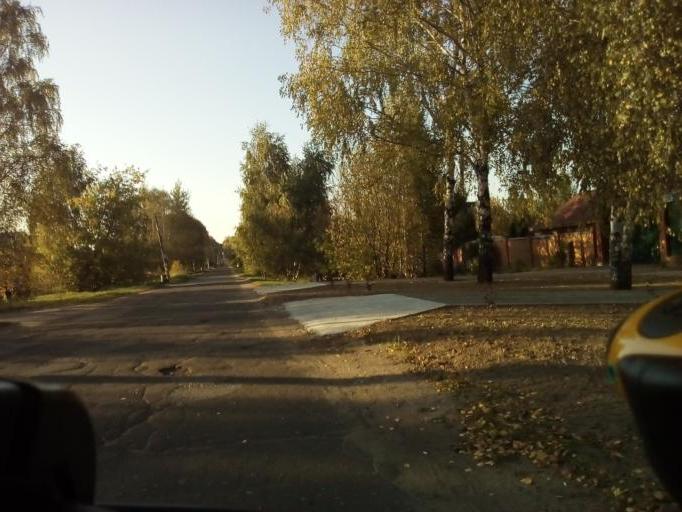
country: RU
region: Moskovskaya
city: Ramenskoye
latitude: 55.6075
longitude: 38.3027
